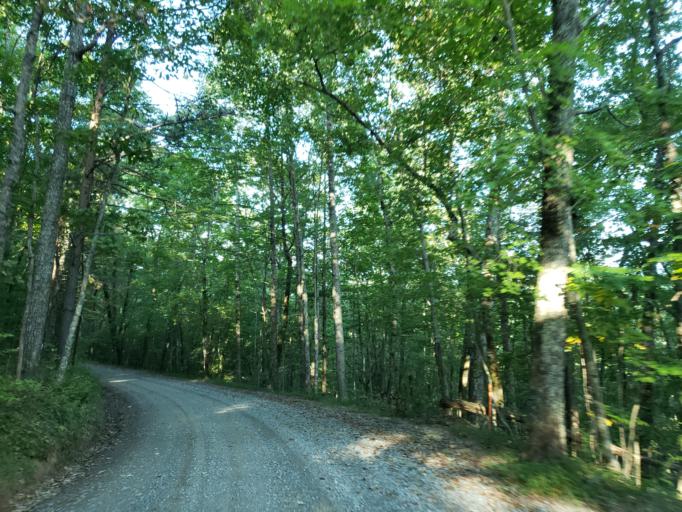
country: US
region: Georgia
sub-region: Fannin County
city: Blue Ridge
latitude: 34.6888
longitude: -84.2668
